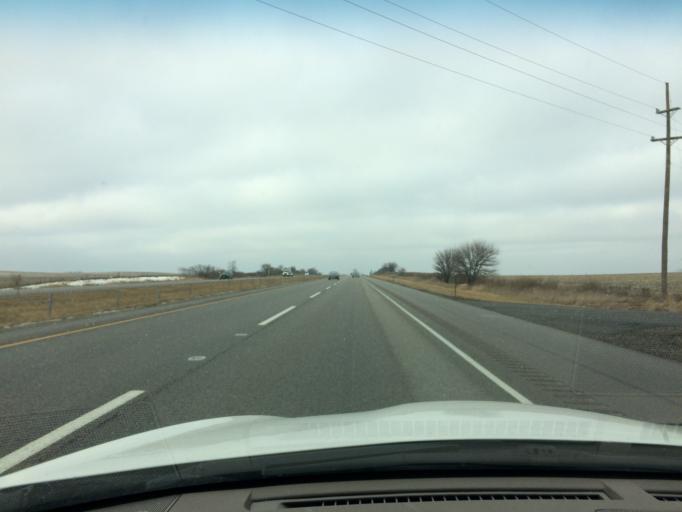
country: US
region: Illinois
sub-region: Kane County
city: Maple Park
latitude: 41.8806
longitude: -88.6203
